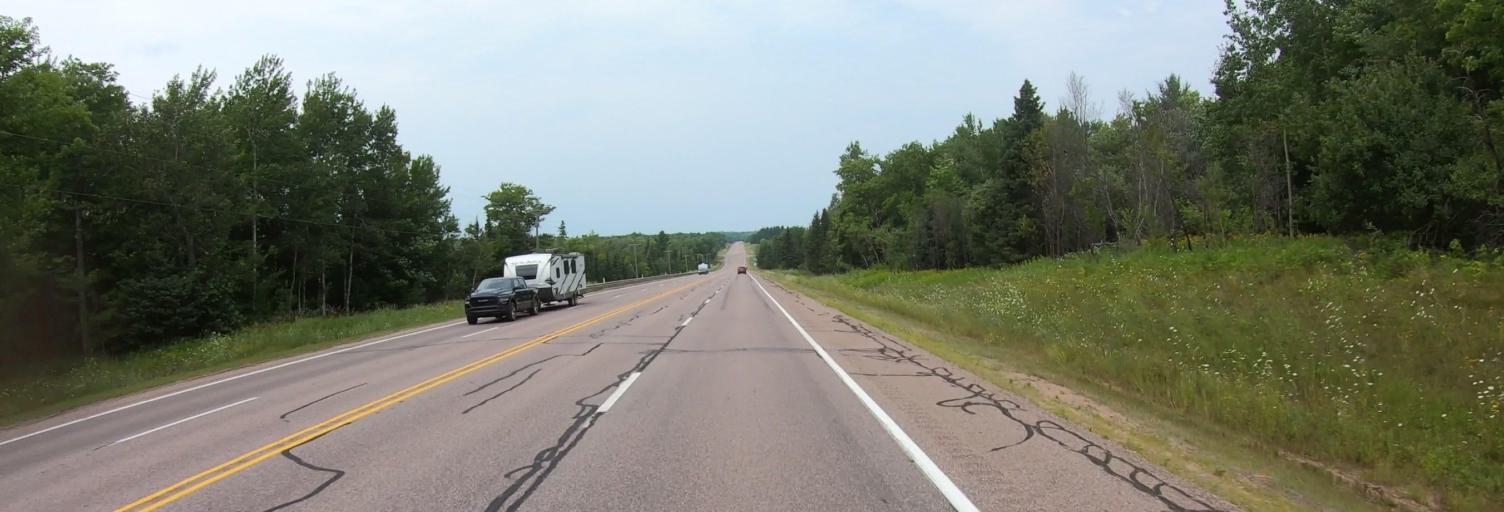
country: US
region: Michigan
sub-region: Marquette County
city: K. I. Sawyer Air Force Base
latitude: 46.3555
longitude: -87.2216
